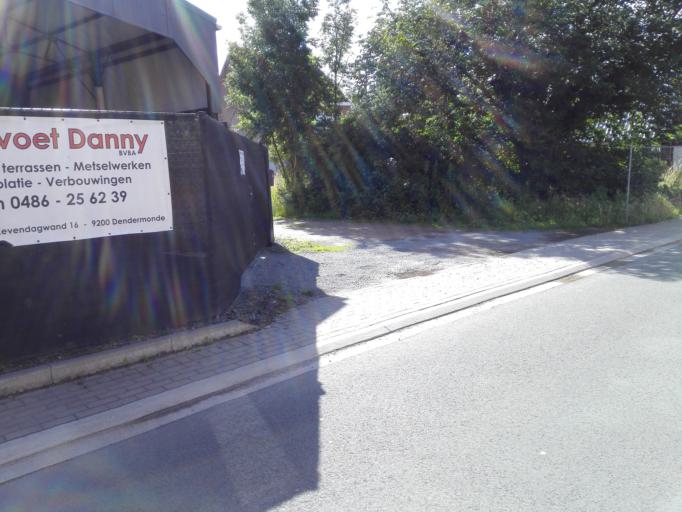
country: BE
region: Flanders
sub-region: Provincie Oost-Vlaanderen
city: Dendermonde
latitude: 51.0281
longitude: 4.1230
